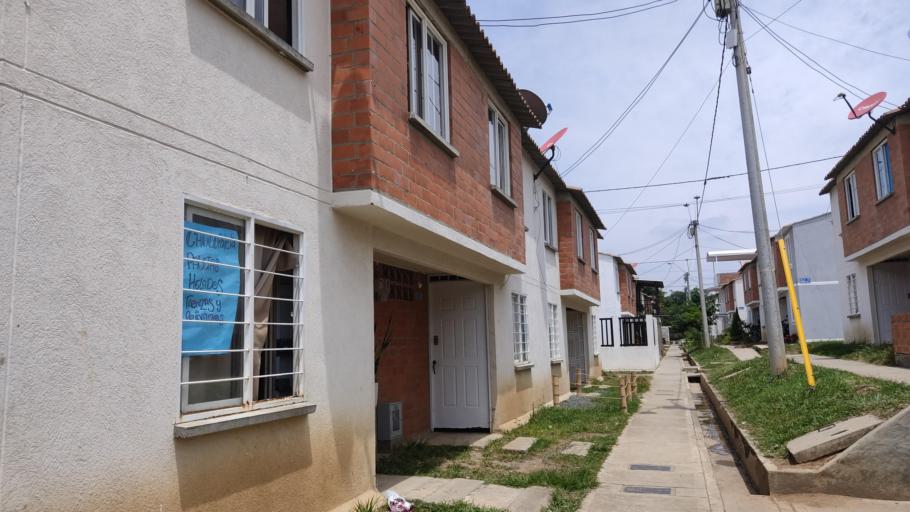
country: CO
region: Valle del Cauca
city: Jamundi
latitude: 3.2359
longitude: -76.5110
